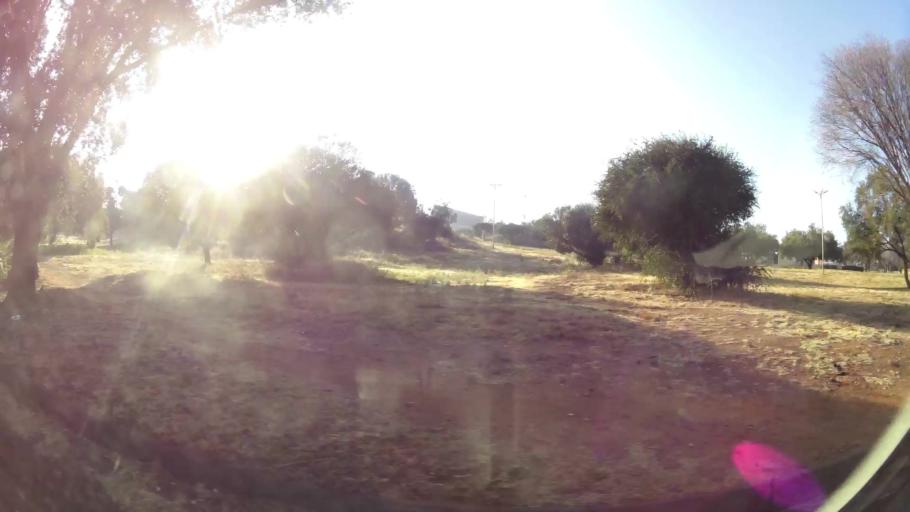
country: ZA
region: Orange Free State
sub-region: Mangaung Metropolitan Municipality
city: Bloemfontein
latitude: -29.1543
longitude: 26.1996
